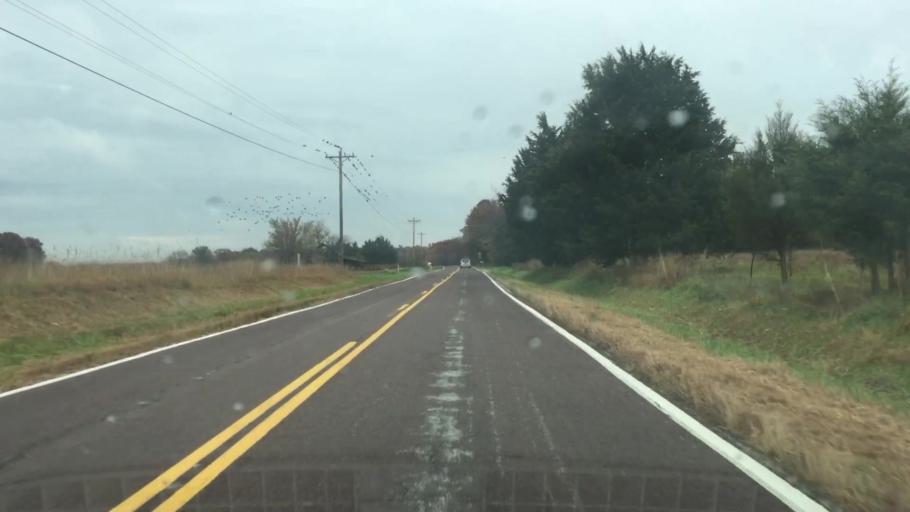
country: US
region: Missouri
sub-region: Callaway County
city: Fulton
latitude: 38.7826
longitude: -91.8198
